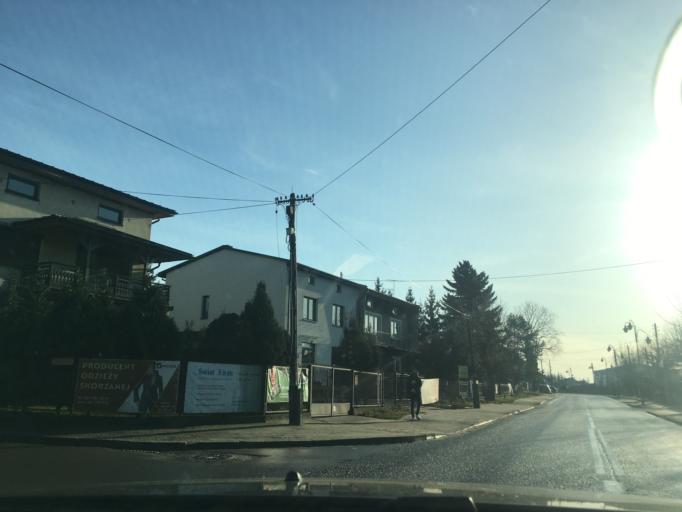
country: PL
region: Swietokrzyskie
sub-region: Powiat jedrzejowski
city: Jedrzejow
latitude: 50.6366
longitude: 20.3059
